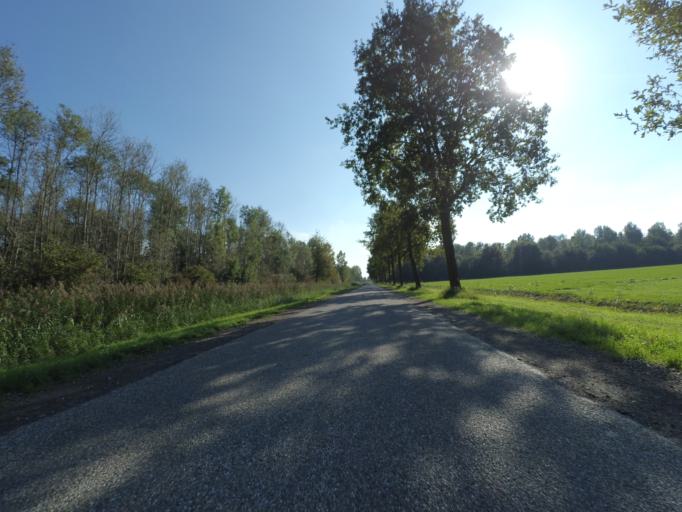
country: NL
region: Flevoland
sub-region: Gemeente Zeewolde
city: Zeewolde
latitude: 52.2808
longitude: 5.5179
